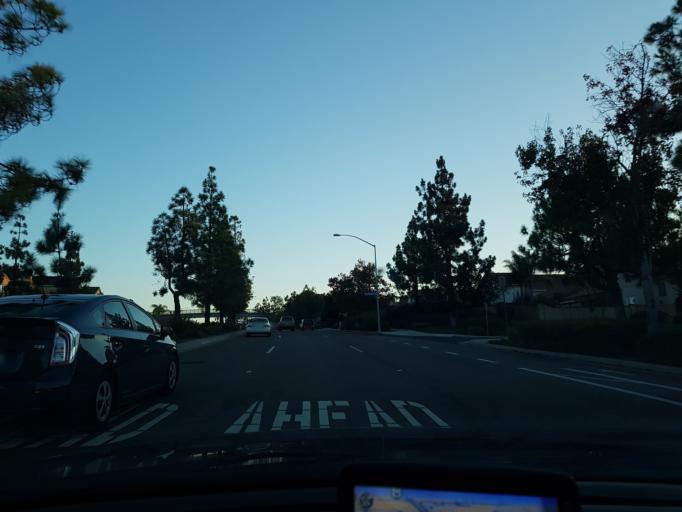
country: US
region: California
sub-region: San Diego County
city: Fairbanks Ranch
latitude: 32.9228
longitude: -117.1250
